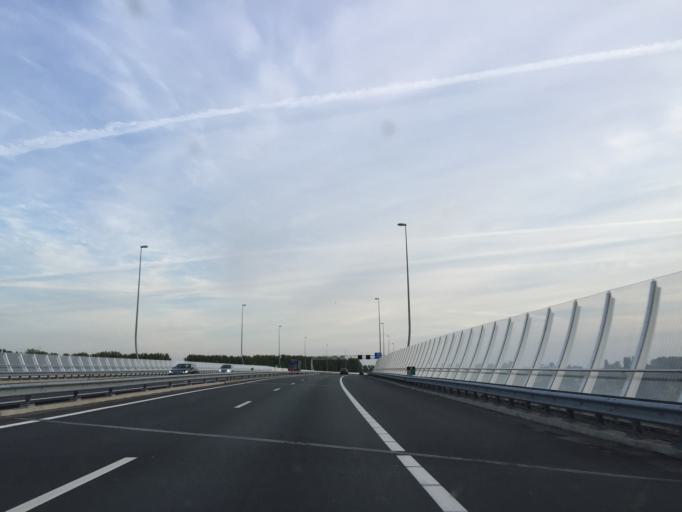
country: NL
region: North Holland
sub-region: Gemeente Zaanstad
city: Zaandam
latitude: 52.3777
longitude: 4.7674
